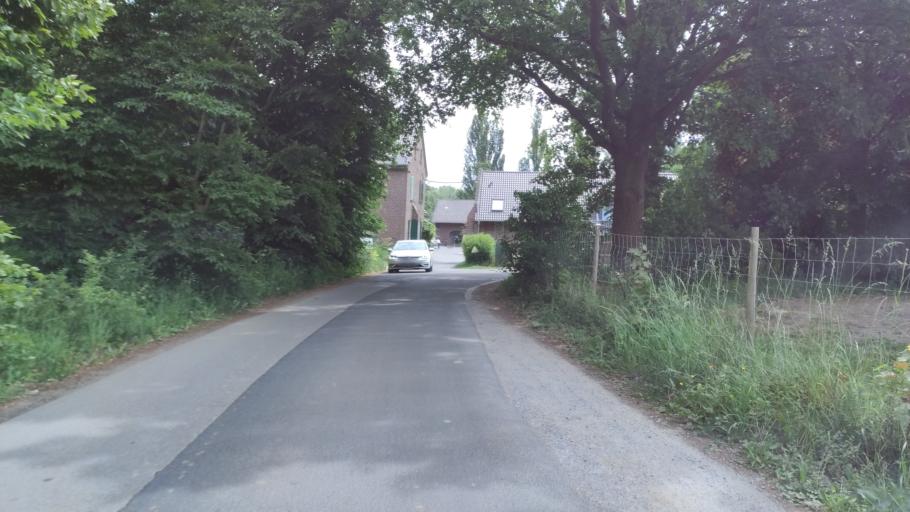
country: DE
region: North Rhine-Westphalia
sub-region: Regierungsbezirk Dusseldorf
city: Neubrueck
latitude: 51.1421
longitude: 6.6550
